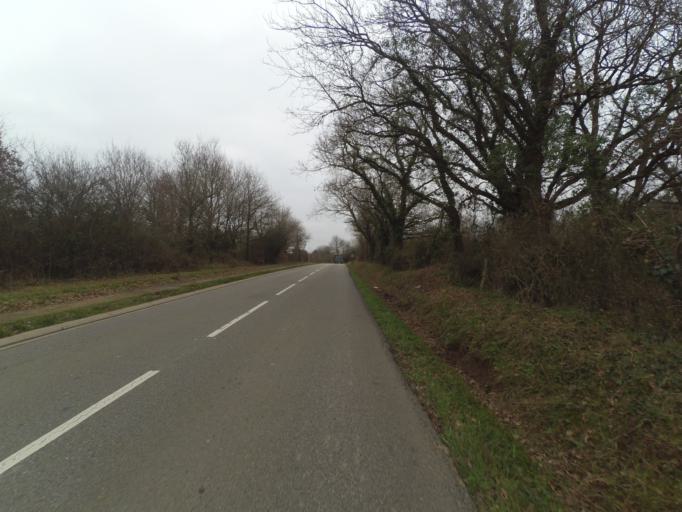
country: FR
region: Pays de la Loire
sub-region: Departement de la Loire-Atlantique
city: Saint-Herblain
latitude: 47.2203
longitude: -1.6586
